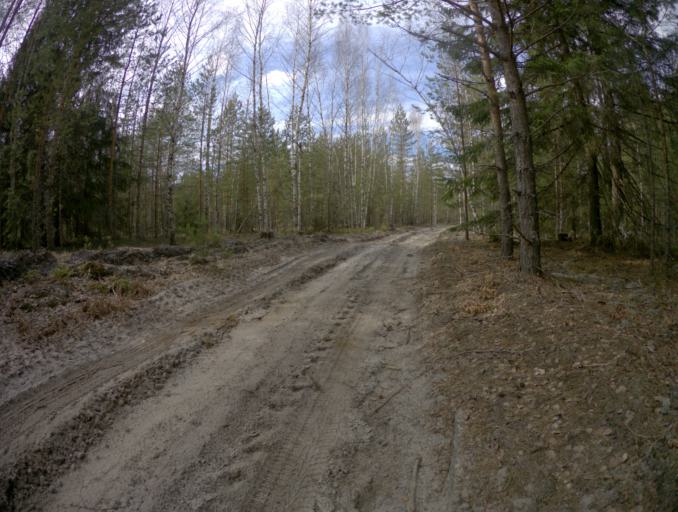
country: RU
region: Vladimir
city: Urshel'skiy
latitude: 55.8685
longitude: 40.1926
